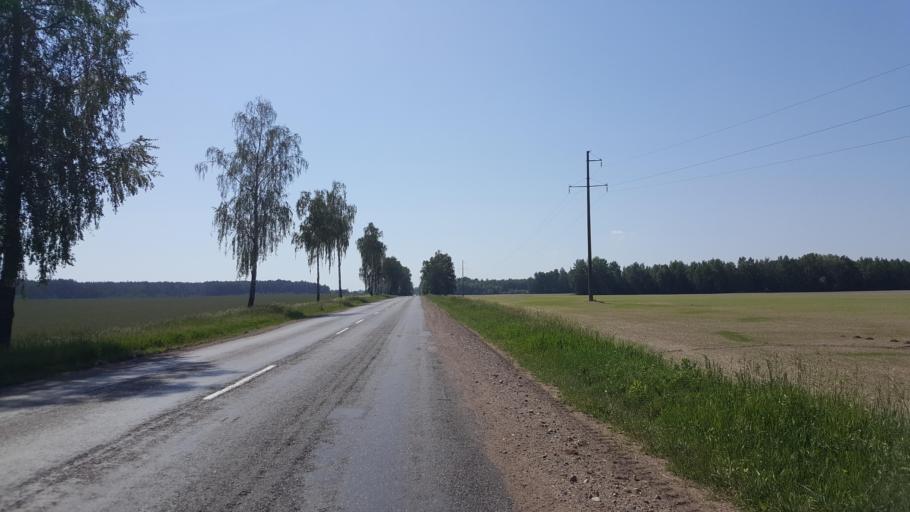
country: BY
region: Brest
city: Zhabinka
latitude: 52.2510
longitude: 23.9696
